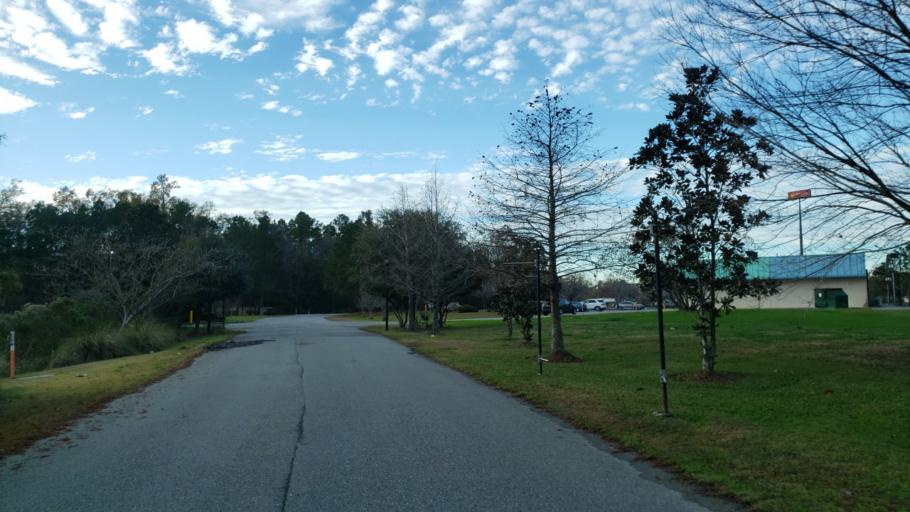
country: US
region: Georgia
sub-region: Chatham County
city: Pooler
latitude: 32.1099
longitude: -81.2389
